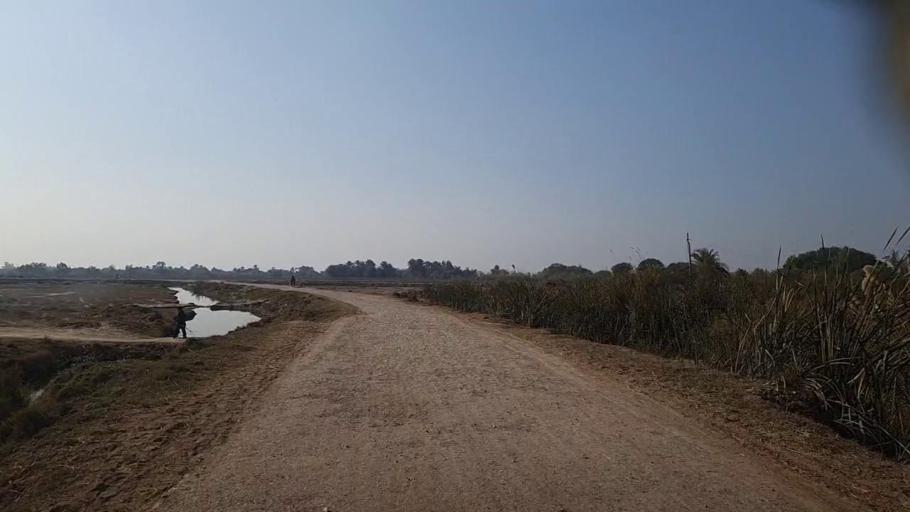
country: PK
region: Sindh
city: Mirpur Mathelo
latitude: 27.8917
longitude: 69.6069
